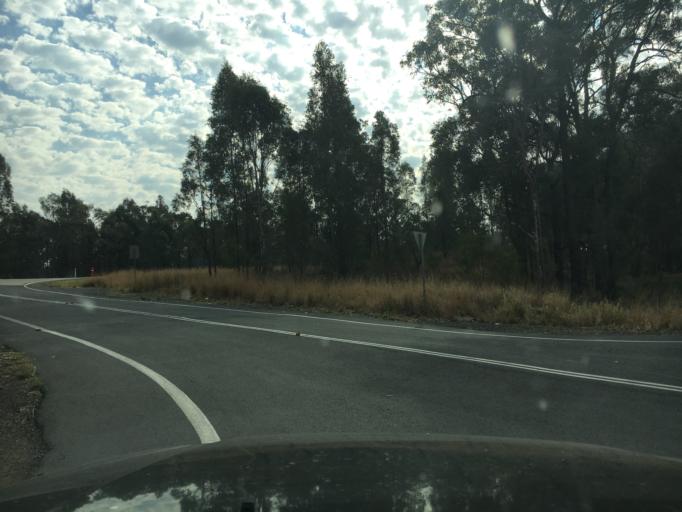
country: AU
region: New South Wales
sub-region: Cessnock
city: Branxton
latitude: -32.6569
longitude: 151.2887
